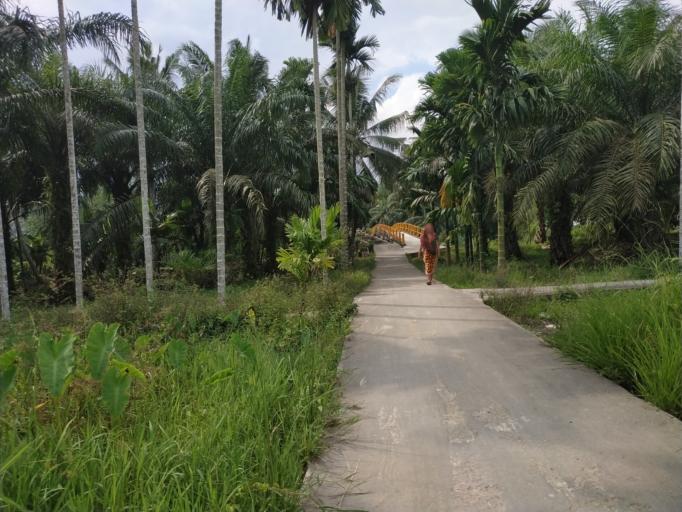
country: ID
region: Riau
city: Sungaisalak
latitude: -0.5161
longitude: 103.0027
